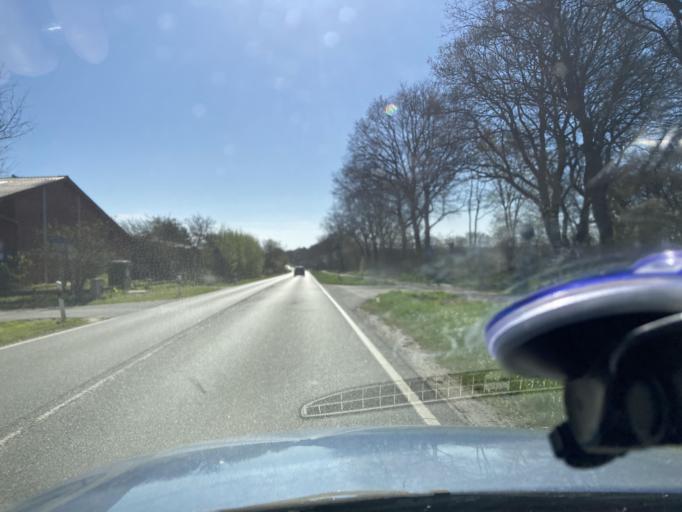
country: DE
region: Schleswig-Holstein
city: Ostrohe
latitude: 54.1959
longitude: 9.1442
